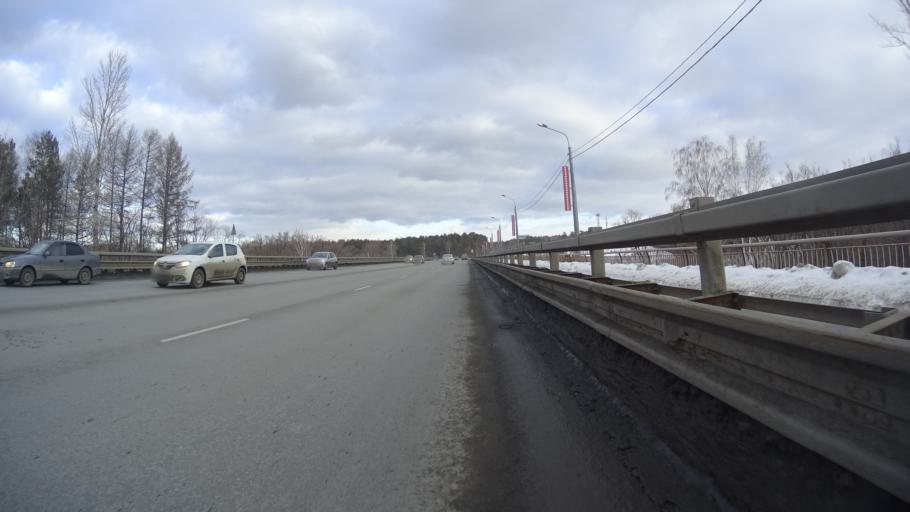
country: RU
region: Chelyabinsk
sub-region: Gorod Chelyabinsk
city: Chelyabinsk
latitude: 55.1484
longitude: 61.3229
